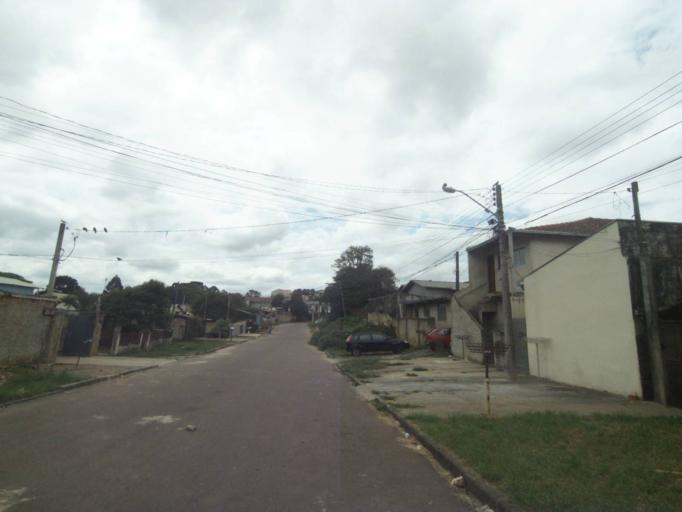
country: BR
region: Parana
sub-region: Curitiba
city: Curitiba
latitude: -25.3896
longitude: -49.2868
